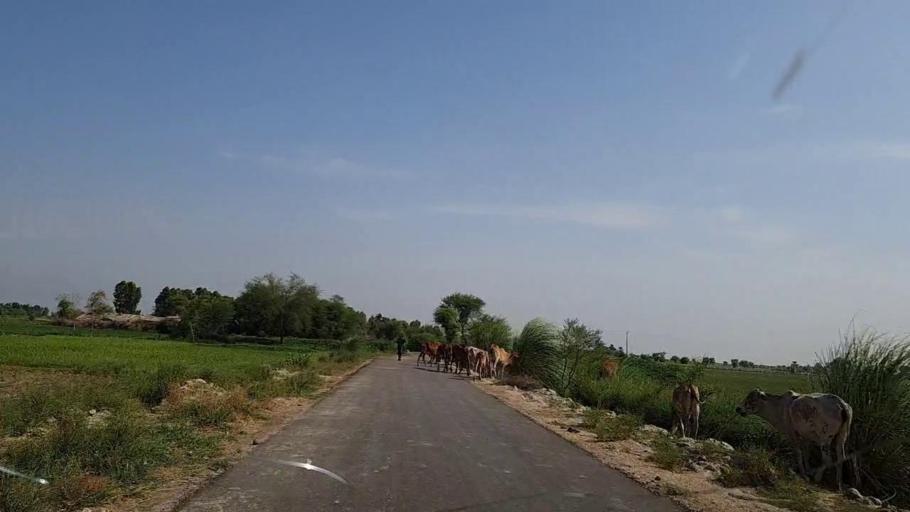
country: PK
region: Sindh
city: Khanpur
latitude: 27.7020
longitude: 69.3638
